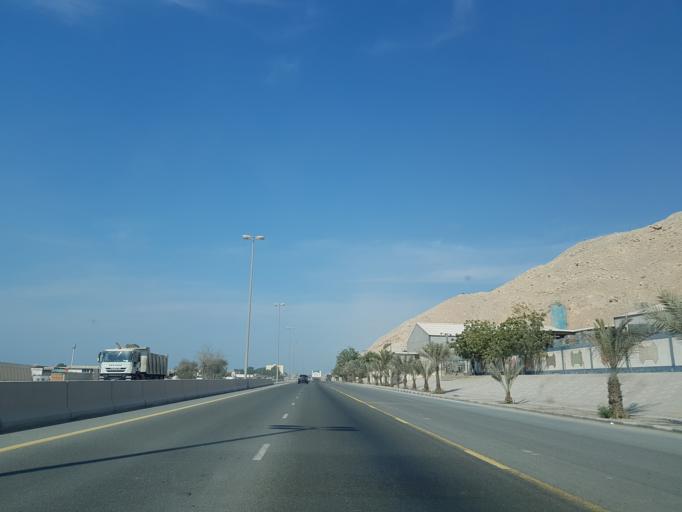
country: AE
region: Ra's al Khaymah
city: Ras al-Khaimah
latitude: 25.8559
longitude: 56.0206
